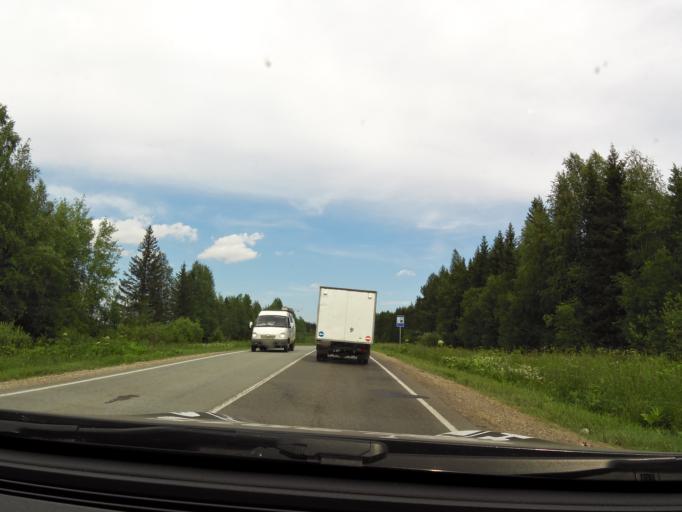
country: RU
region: Kirov
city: Vakhrushi
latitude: 58.6935
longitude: 50.0672
